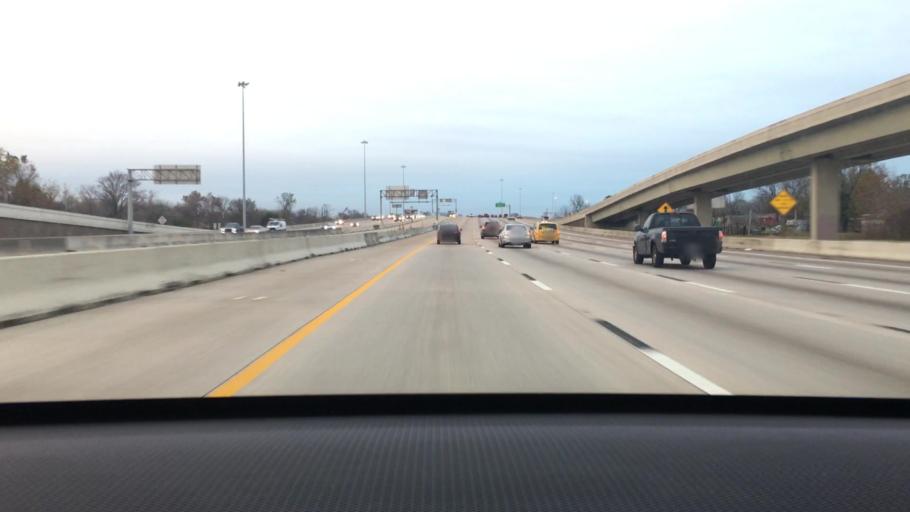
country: US
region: Texas
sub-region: Harris County
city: Aldine
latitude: 29.8549
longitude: -95.3335
